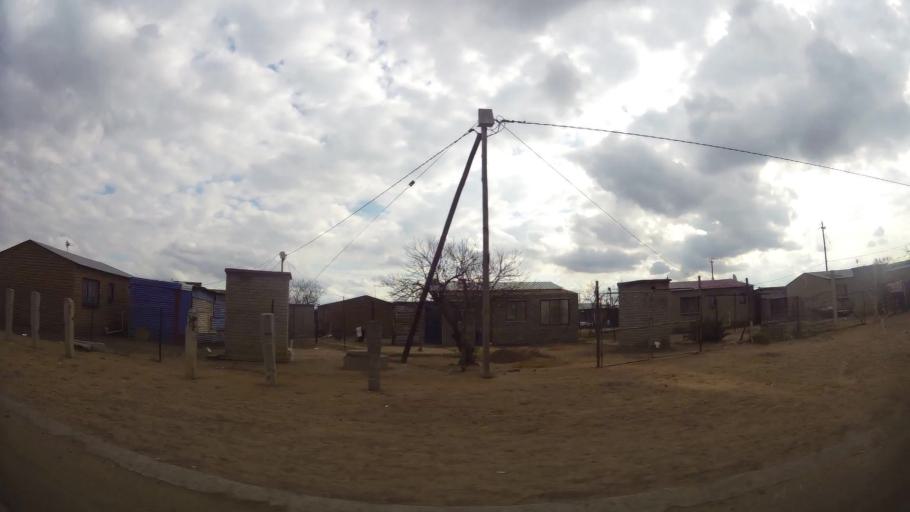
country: ZA
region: Orange Free State
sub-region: Fezile Dabi District Municipality
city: Sasolburg
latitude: -26.8609
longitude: 27.8526
